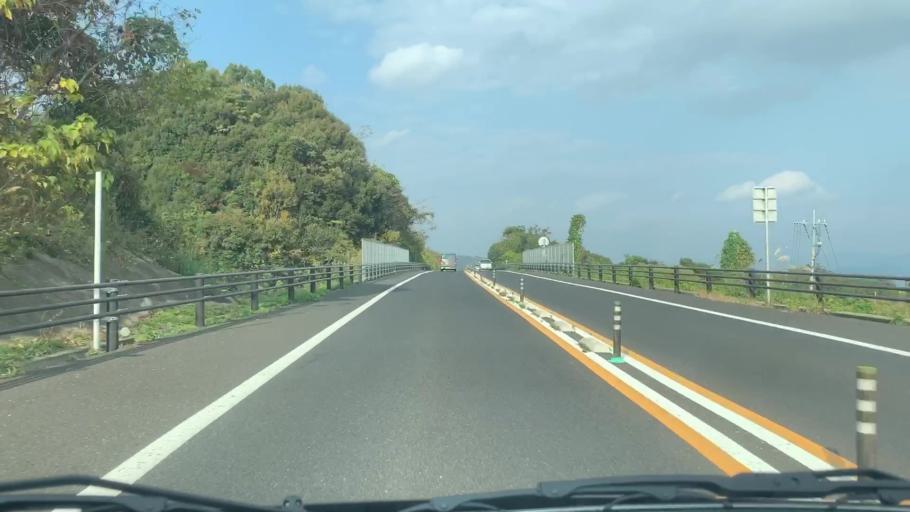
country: JP
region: Nagasaki
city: Sasebo
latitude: 33.0072
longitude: 129.7279
